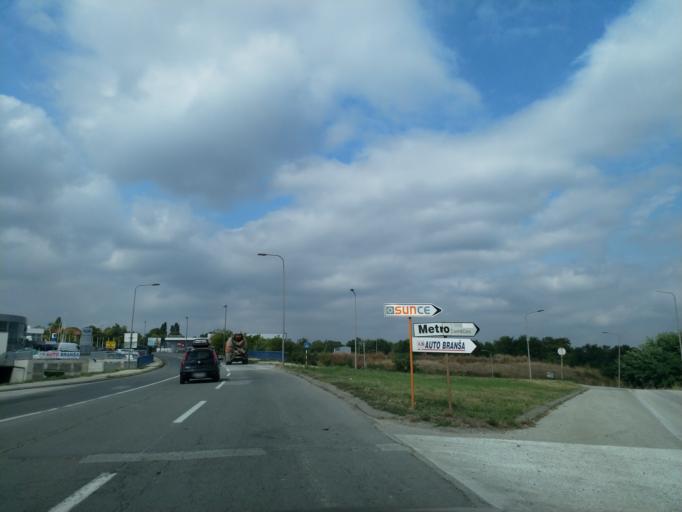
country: RS
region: Central Serbia
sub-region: Sumadijski Okrug
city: Kragujevac
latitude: 44.0226
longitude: 20.9313
